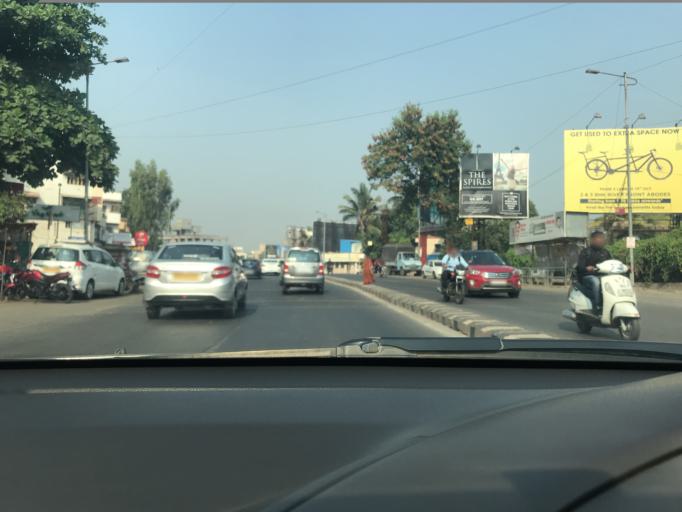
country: IN
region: Maharashtra
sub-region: Pune Division
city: Khadki
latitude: 18.5544
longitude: 73.8015
